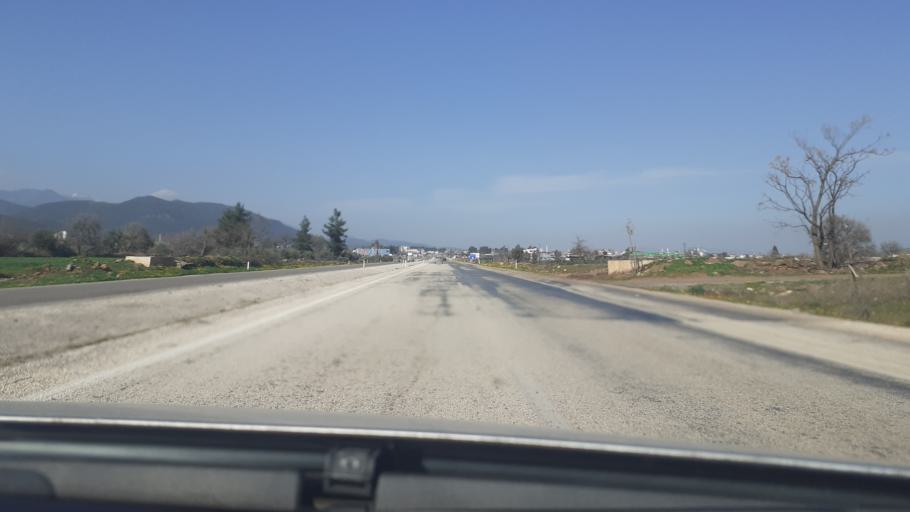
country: TR
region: Hatay
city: Aktepe
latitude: 36.6838
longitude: 36.4707
